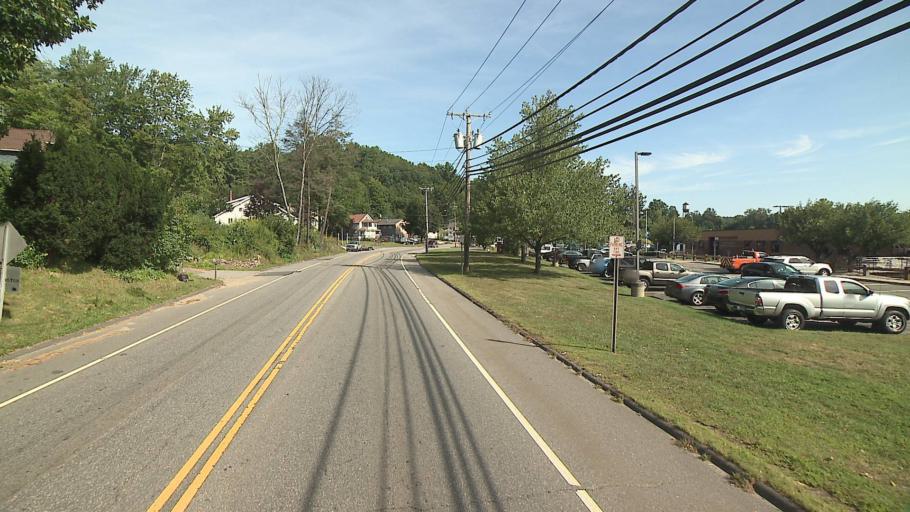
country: US
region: Connecticut
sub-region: Litchfield County
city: Thomaston
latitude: 41.6648
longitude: -73.0797
